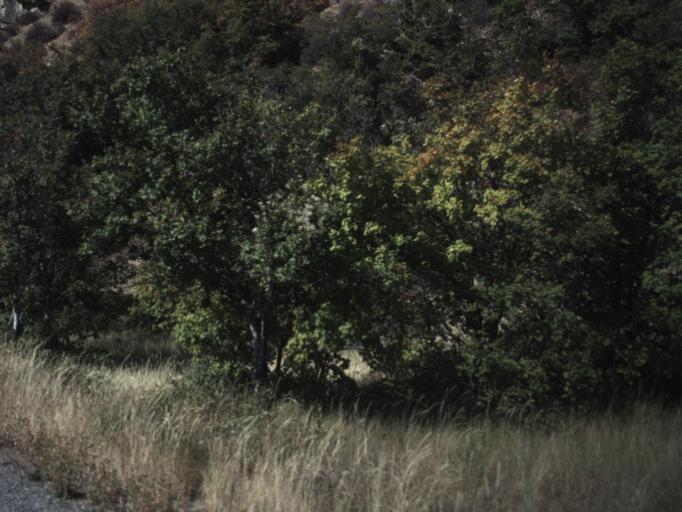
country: US
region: Utah
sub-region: Cache County
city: Millville
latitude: 41.6215
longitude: -111.7587
